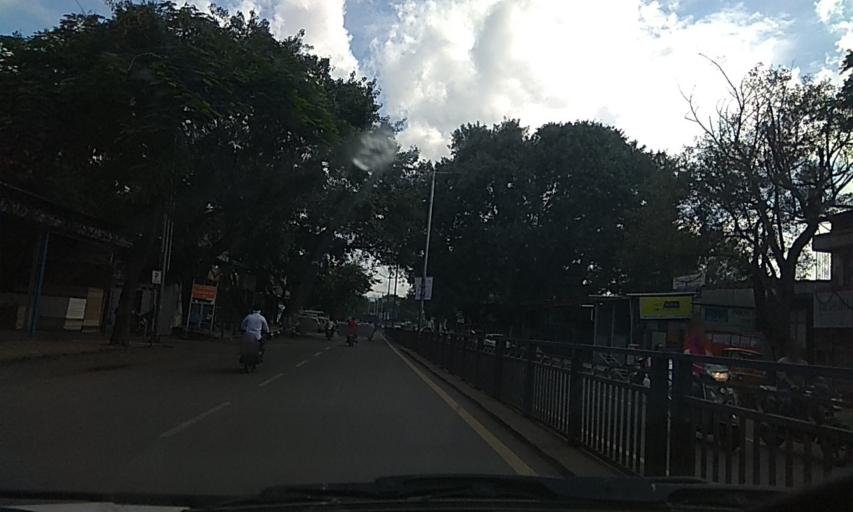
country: IN
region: Maharashtra
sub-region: Pune Division
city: Pune
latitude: 18.5096
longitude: 73.8682
